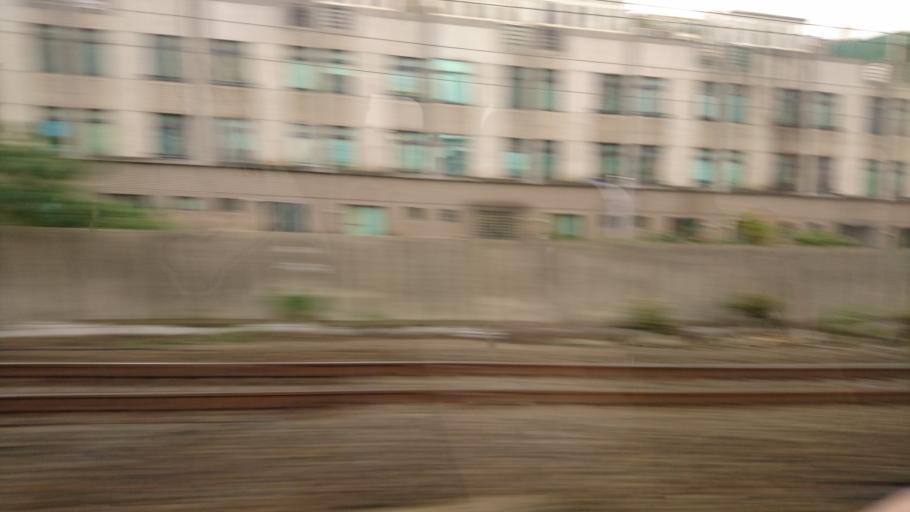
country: TW
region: Taiwan
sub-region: Hsinchu
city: Zhubei
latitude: 24.8342
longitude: 121.0056
